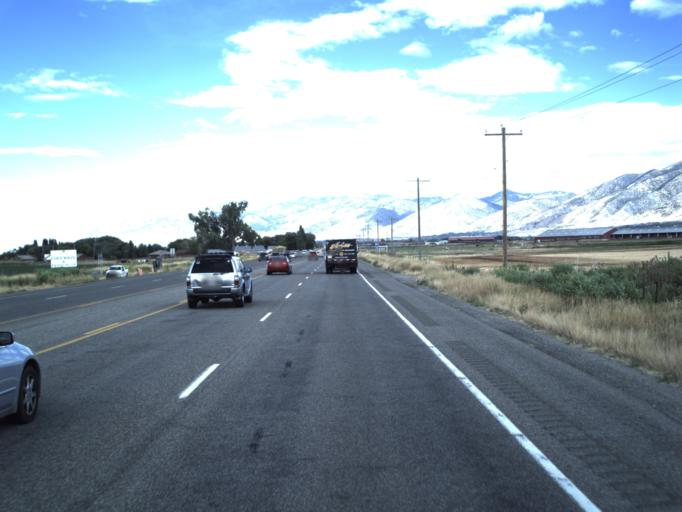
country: US
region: Utah
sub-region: Cache County
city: Wellsville
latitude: 41.6521
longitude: -111.9066
